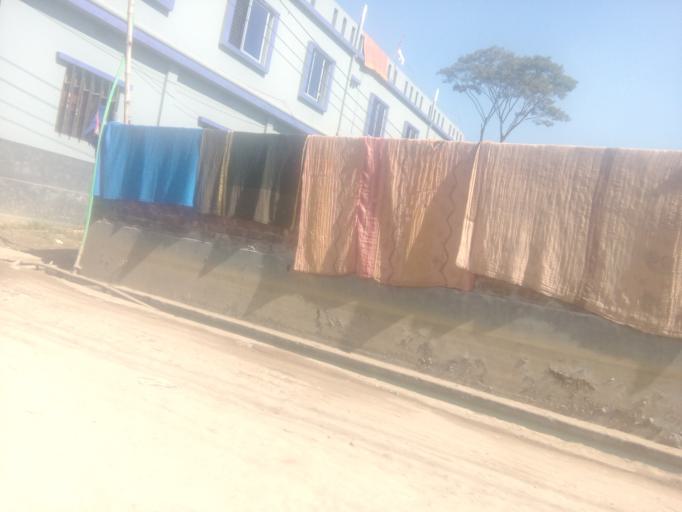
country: BD
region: Dhaka
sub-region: Dhaka
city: Dhaka
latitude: 23.7061
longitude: 90.4755
